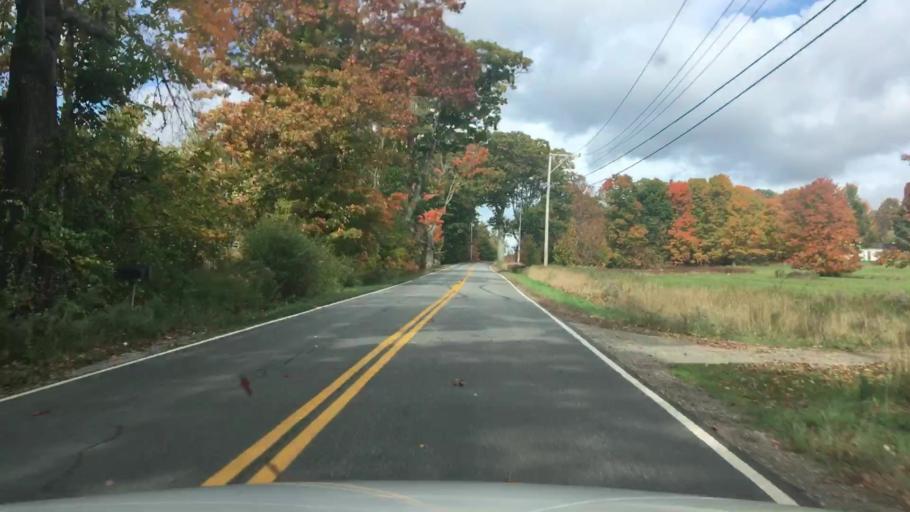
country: US
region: Maine
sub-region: Knox County
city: Hope
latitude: 44.3028
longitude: -69.1125
